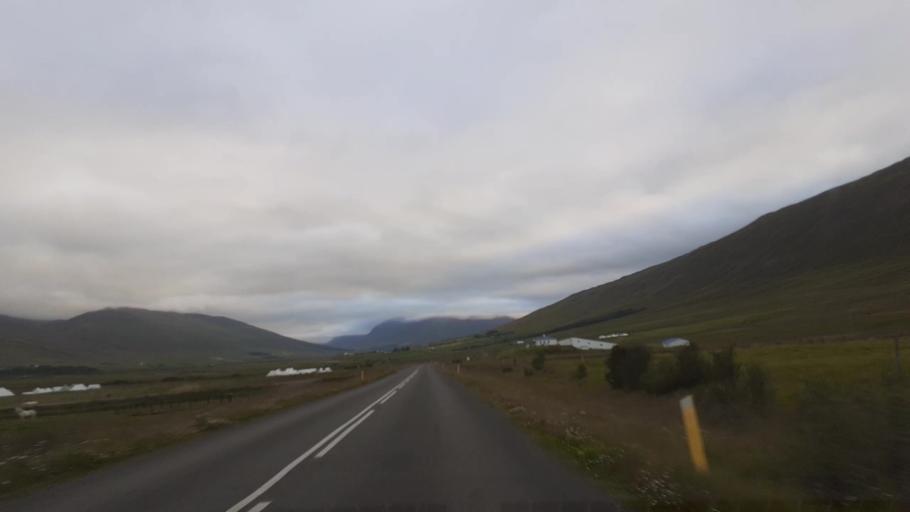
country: IS
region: Northeast
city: Dalvik
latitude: 65.9500
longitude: -18.5548
